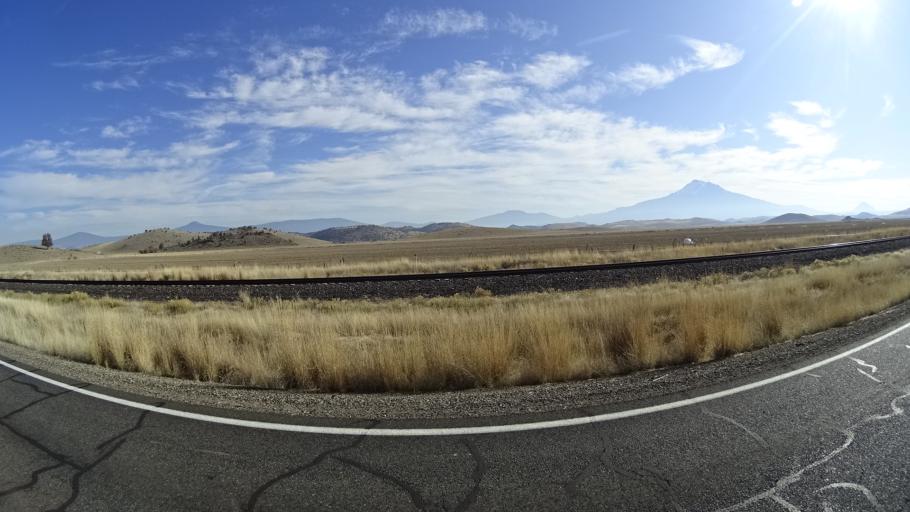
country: US
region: California
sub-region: Siskiyou County
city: Montague
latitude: 41.5795
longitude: -122.5247
